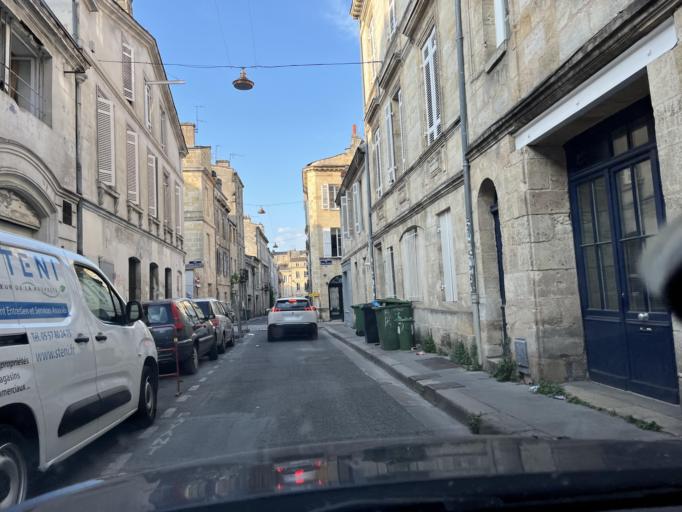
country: FR
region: Aquitaine
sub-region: Departement de la Gironde
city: Bordeaux
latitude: 44.8329
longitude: -0.5646
